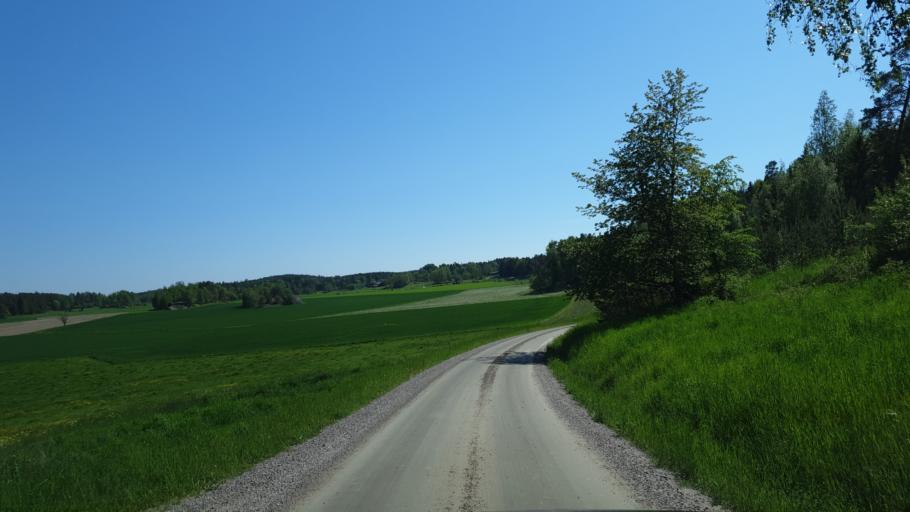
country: SE
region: Soedermanland
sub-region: Trosa Kommun
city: Vagnharad
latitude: 58.9313
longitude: 17.5169
